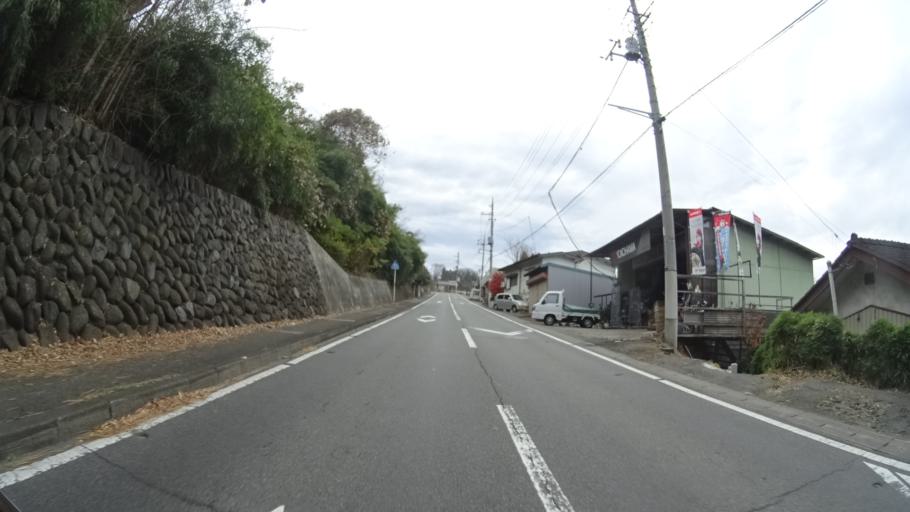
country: JP
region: Gunma
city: Numata
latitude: 36.6473
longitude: 139.0378
